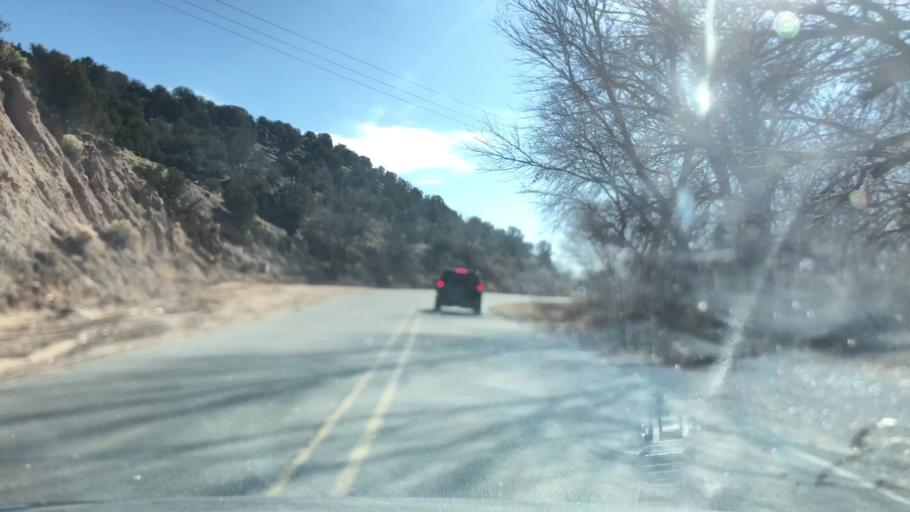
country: US
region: New Mexico
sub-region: Rio Arriba County
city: Ohkay Owingeh
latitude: 36.0867
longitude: -106.1276
